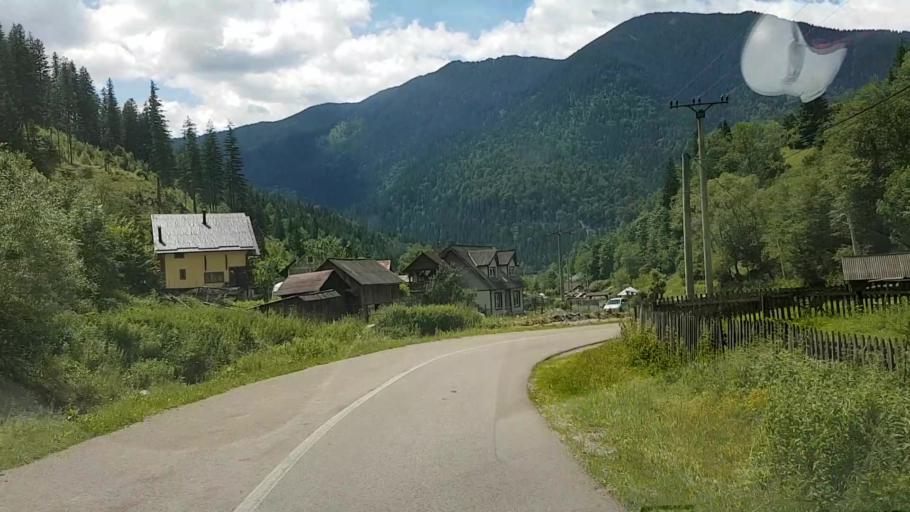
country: RO
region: Suceava
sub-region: Comuna Crucea
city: Crucea
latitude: 47.4045
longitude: 25.5743
